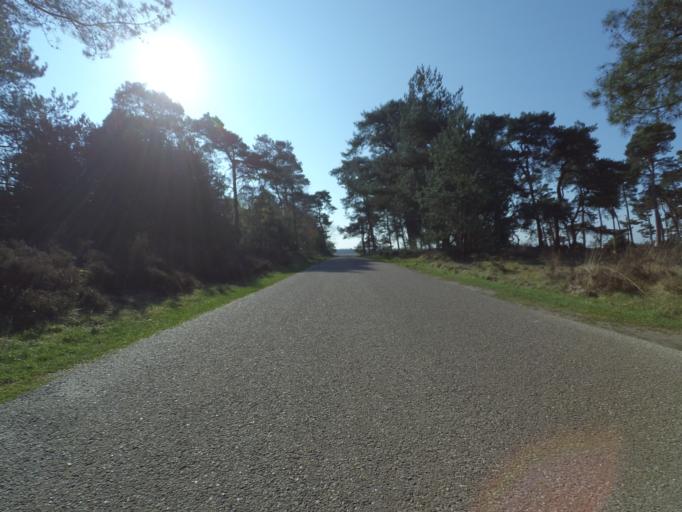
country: NL
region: Gelderland
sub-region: Gemeente Renkum
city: Wolfheze
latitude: 52.0598
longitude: 5.8336
